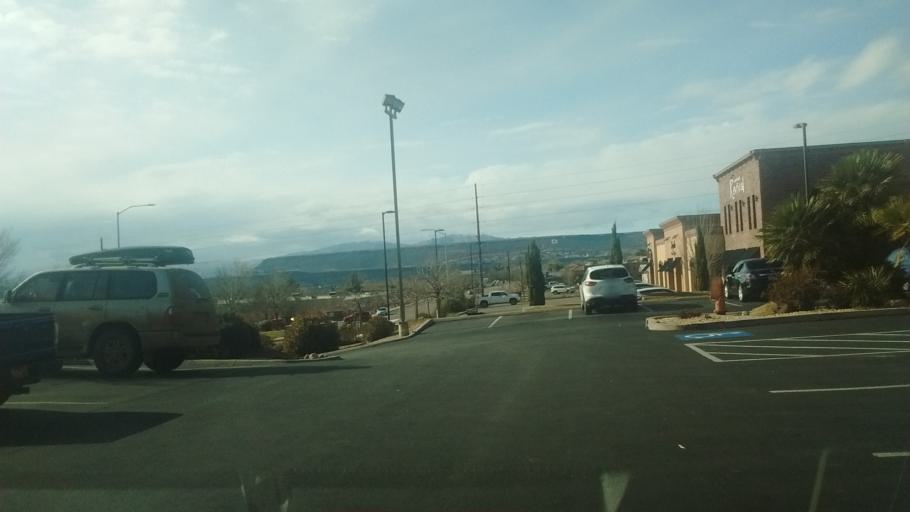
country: US
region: Utah
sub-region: Washington County
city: Saint George
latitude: 37.1083
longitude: -113.5607
